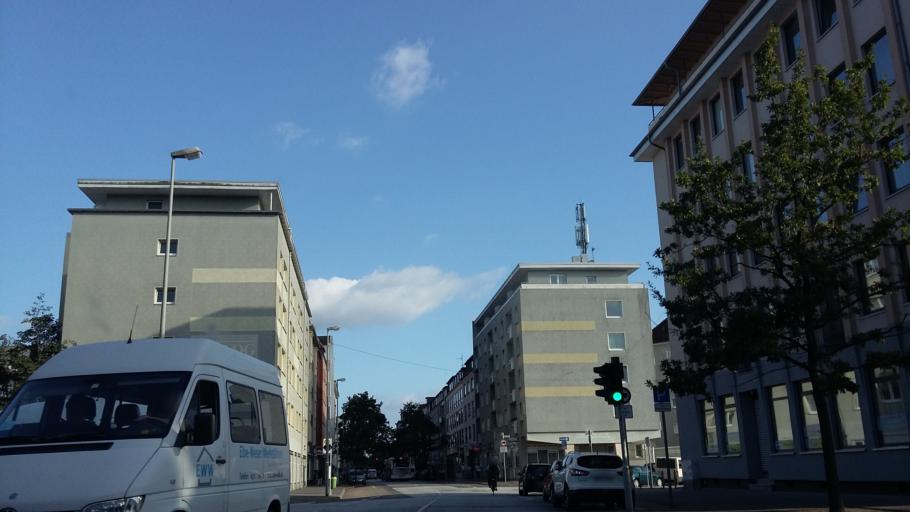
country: DE
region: Bremen
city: Bremerhaven
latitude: 53.5503
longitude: 8.5727
